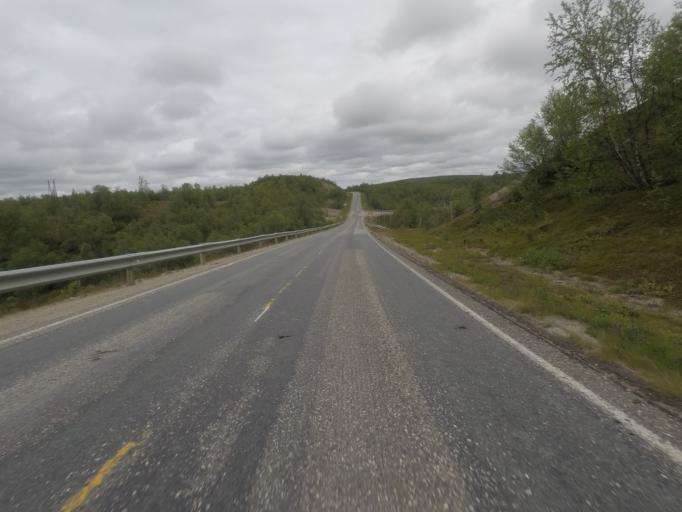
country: NO
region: Finnmark Fylke
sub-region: Kautokeino
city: Kautokeino
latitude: 69.1949
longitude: 23.5600
